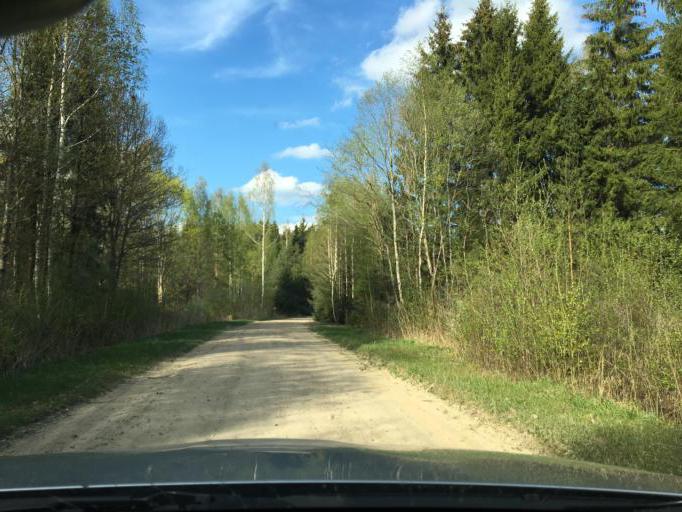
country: LV
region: Ozolnieku
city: Ozolnieki
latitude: 56.6618
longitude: 23.8688
